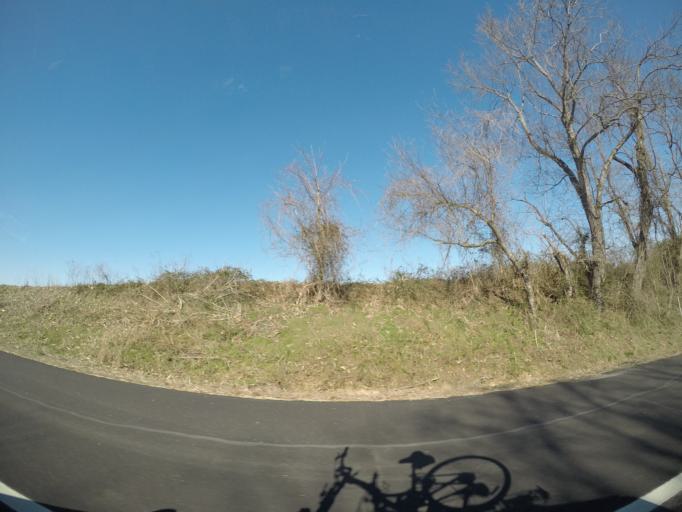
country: US
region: Delaware
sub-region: New Castle County
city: Townsend
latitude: 39.3636
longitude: -75.8226
